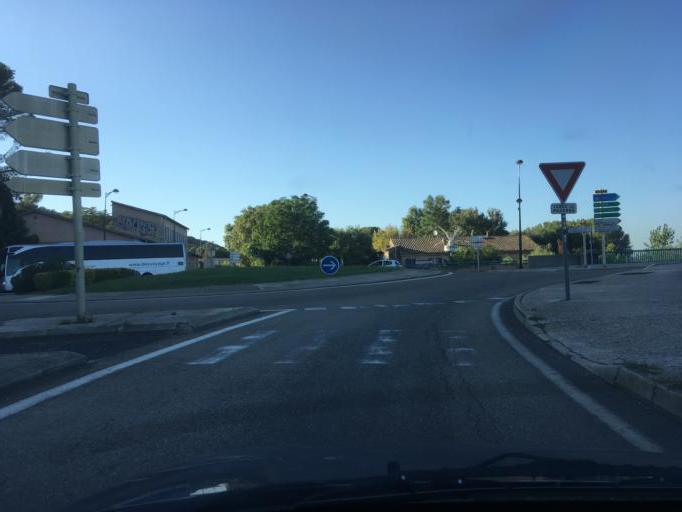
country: FR
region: Languedoc-Roussillon
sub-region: Departement du Gard
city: Remoulins
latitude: 43.9366
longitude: 4.5562
